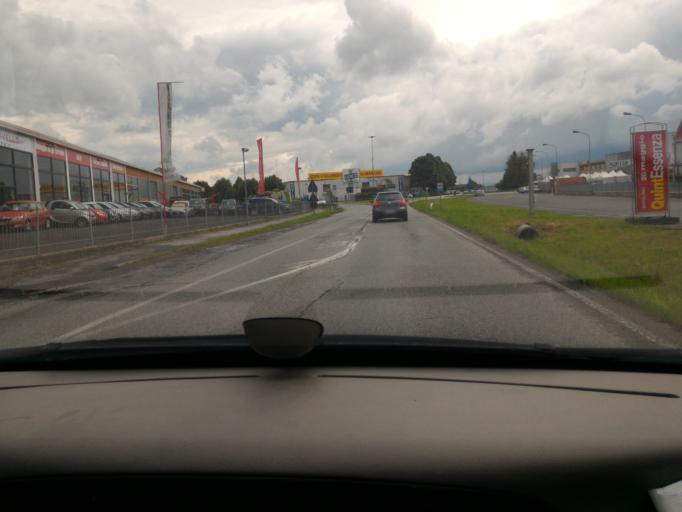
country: IT
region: Piedmont
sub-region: Provincia di Cuneo
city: Genola
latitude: 44.5965
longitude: 7.6592
